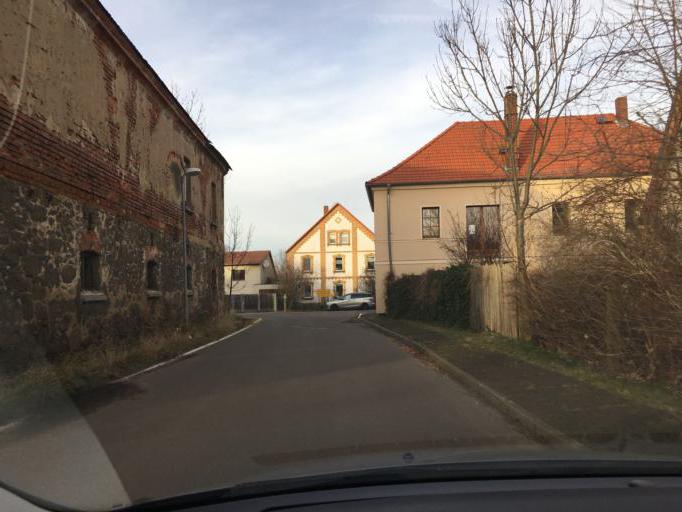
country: DE
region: Saxony
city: Belgershain
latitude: 51.2092
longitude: 12.5245
